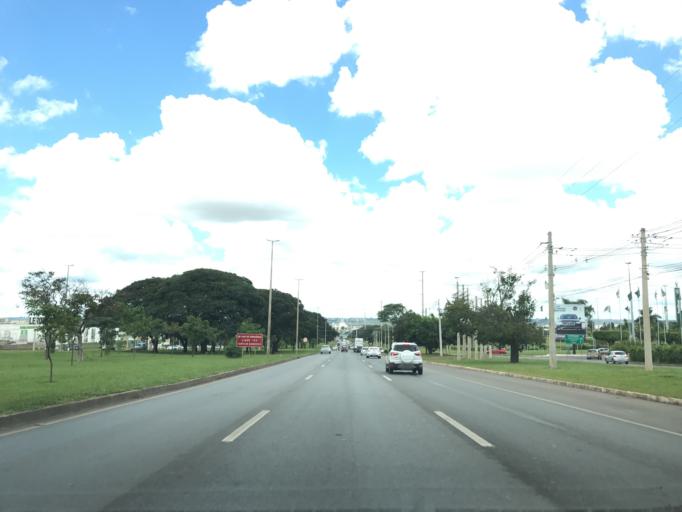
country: BR
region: Federal District
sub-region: Brasilia
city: Brasilia
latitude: -15.8323
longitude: -47.9522
